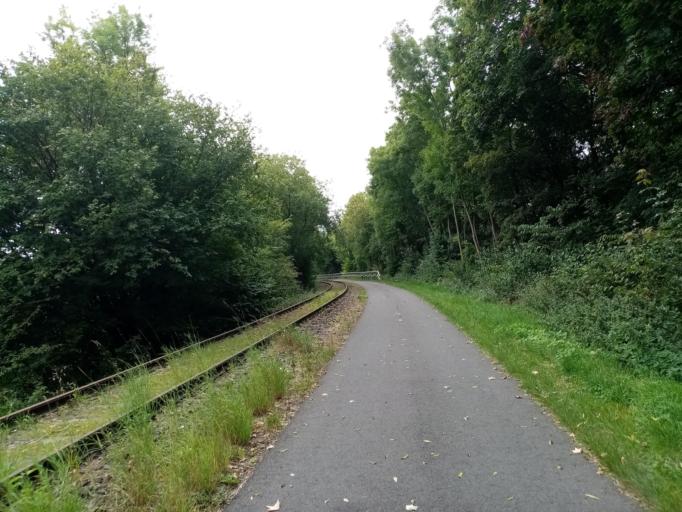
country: DE
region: Thuringia
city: Kefferhausen
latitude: 51.3195
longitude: 10.2975
